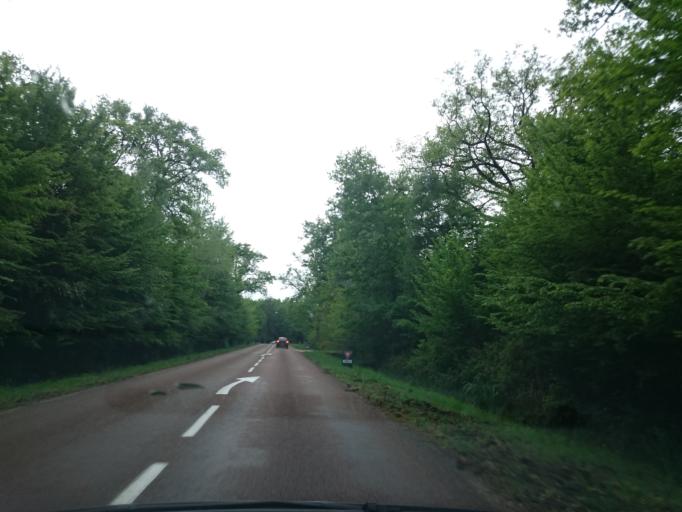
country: FR
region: Centre
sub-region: Departement du Loir-et-Cher
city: Saint-Dye-sur-Loire
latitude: 47.6238
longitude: 1.5097
